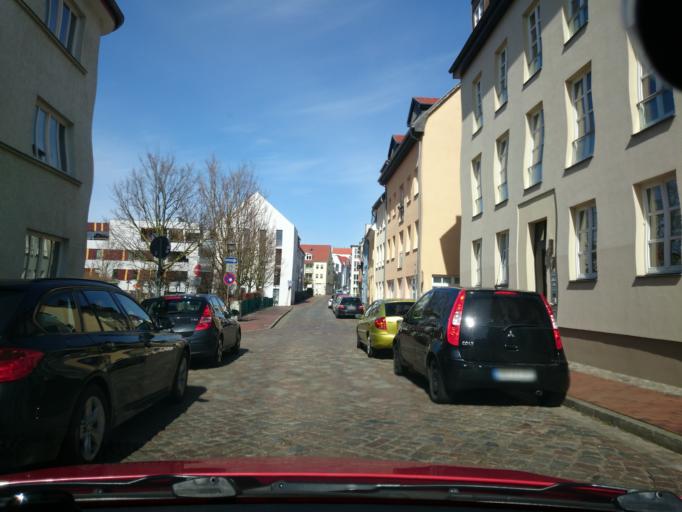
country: DE
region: Mecklenburg-Vorpommern
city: Rostock
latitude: 54.0891
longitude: 12.1454
